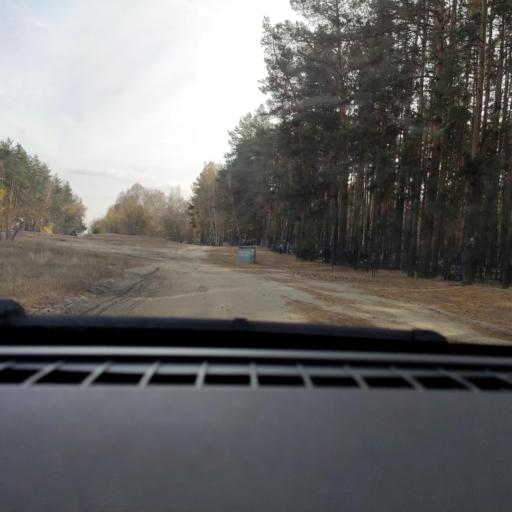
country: RU
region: Voronezj
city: Maslovka
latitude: 51.5778
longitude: 39.2936
